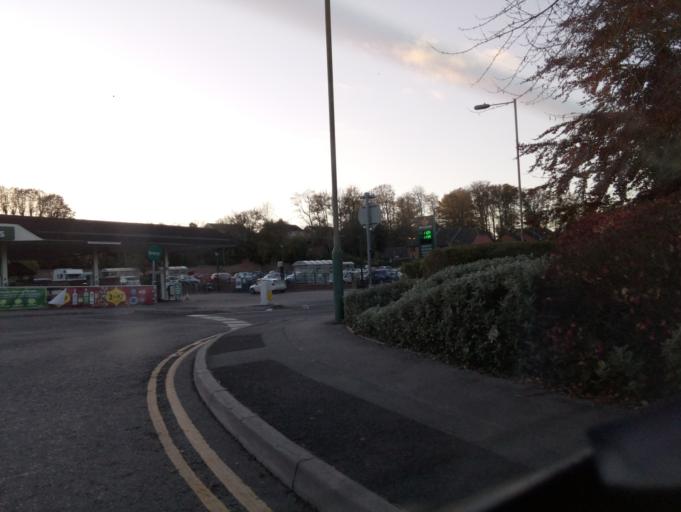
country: GB
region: England
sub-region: Wiltshire
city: Warminster
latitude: 51.2033
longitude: -2.1826
